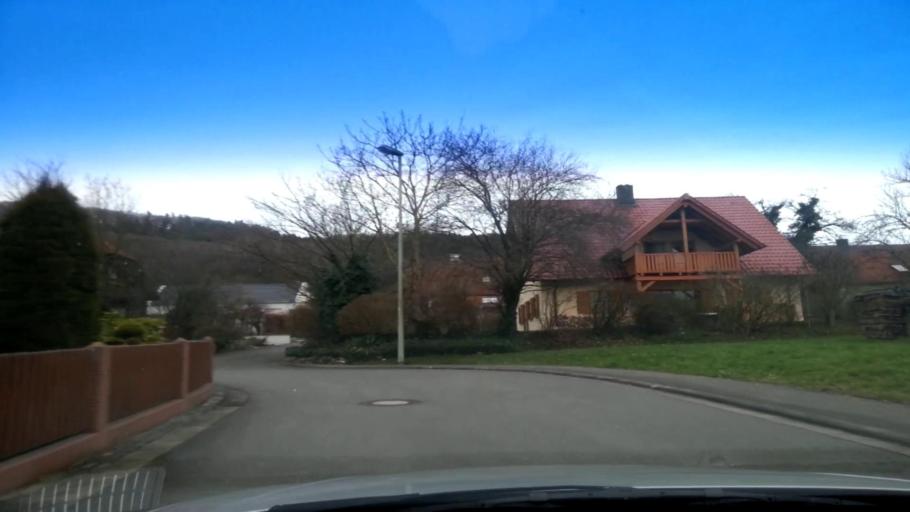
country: DE
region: Bavaria
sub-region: Upper Franconia
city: Litzendorf
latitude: 49.8808
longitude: 11.0198
